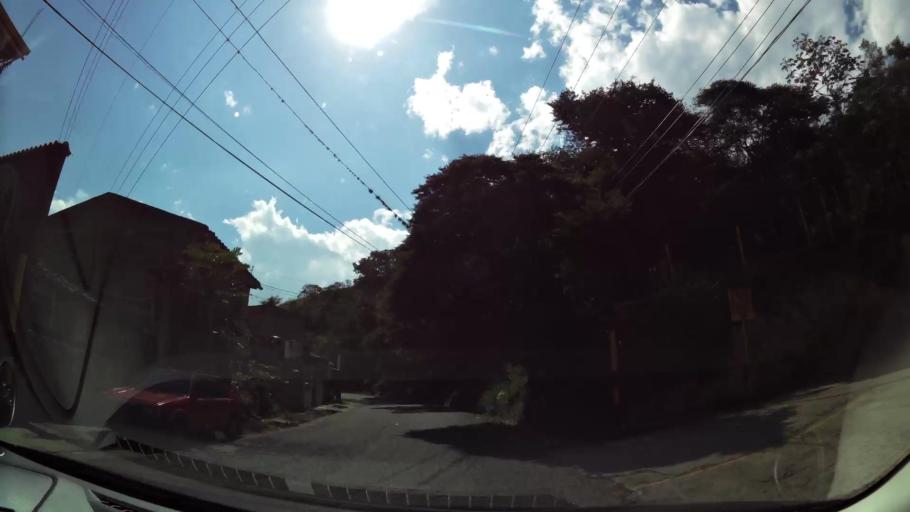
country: CO
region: Valle del Cauca
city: Cali
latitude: 3.4385
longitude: -76.5538
